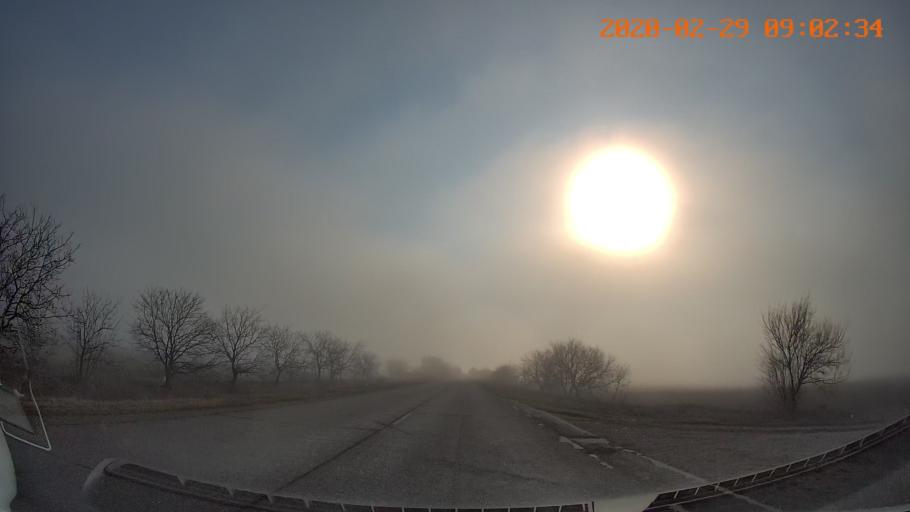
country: UA
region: Odessa
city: Velykoploske
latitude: 46.9202
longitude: 29.7129
